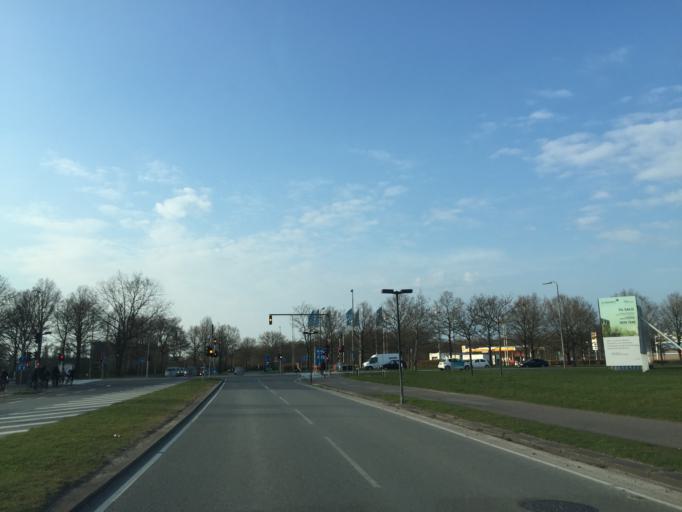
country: DK
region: South Denmark
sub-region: Odense Kommune
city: Neder Holluf
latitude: 55.3750
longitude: 10.4287
